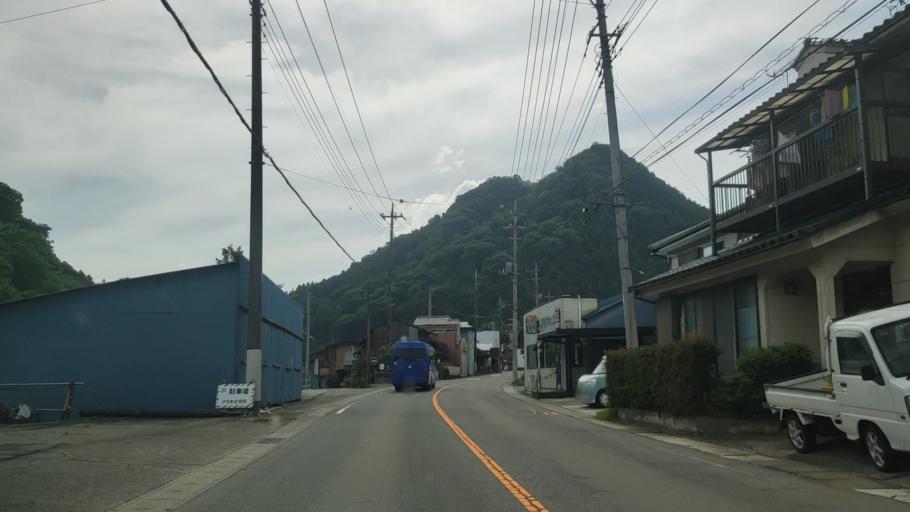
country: JP
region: Gunma
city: Tomioka
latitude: 36.2078
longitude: 138.7810
